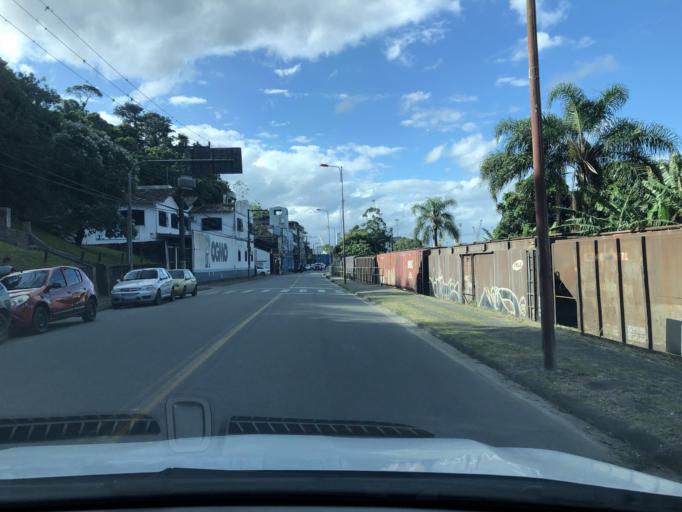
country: BR
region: Santa Catarina
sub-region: Sao Francisco Do Sul
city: Sao Francisco do Sul
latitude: -26.2442
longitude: -48.6348
